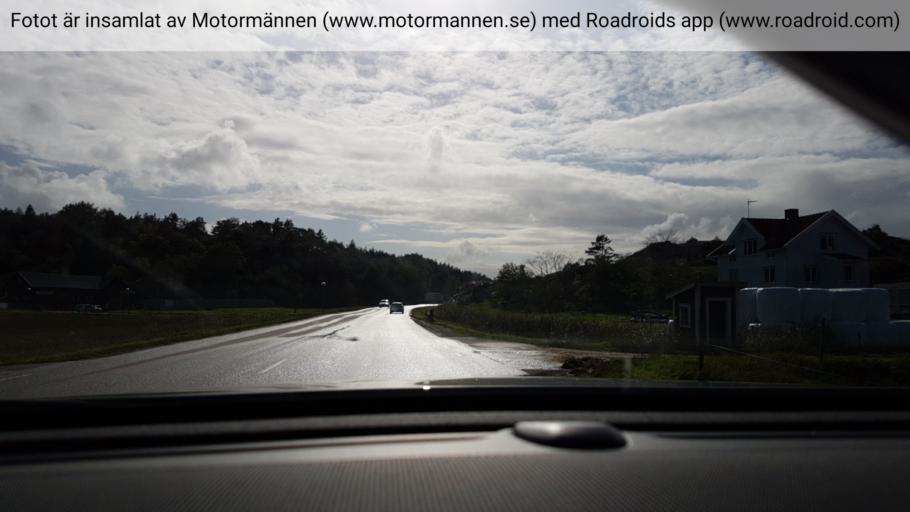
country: SE
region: Vaestra Goetaland
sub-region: Tjorns Kommun
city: Skaerhamn
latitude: 57.9946
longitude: 11.5868
